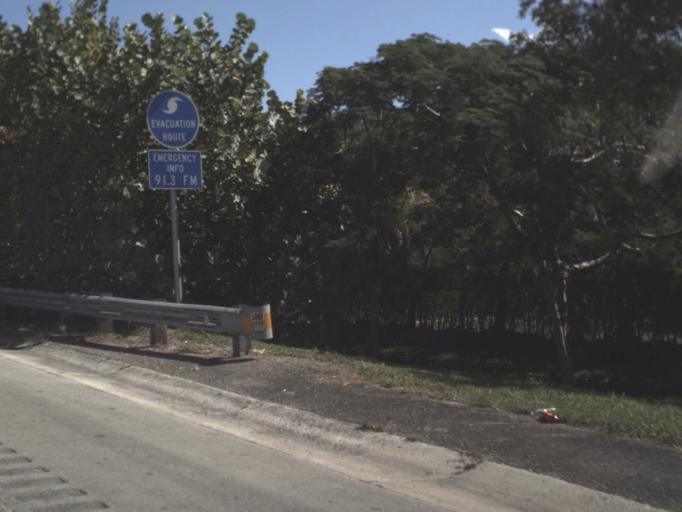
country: US
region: Florida
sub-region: Miami-Dade County
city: Homestead
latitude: 25.4609
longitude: -80.4643
